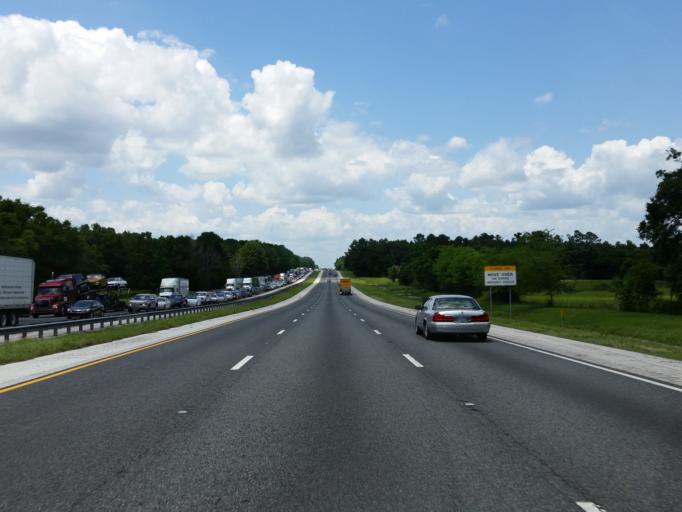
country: US
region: Florida
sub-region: Marion County
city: Citra
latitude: 29.3771
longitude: -82.2311
